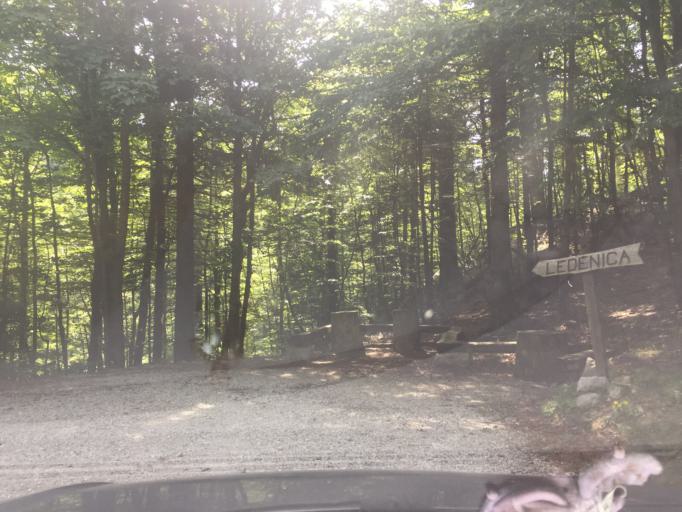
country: SI
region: Ajdovscina
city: Lokavec
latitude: 45.9884
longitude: 13.8426
